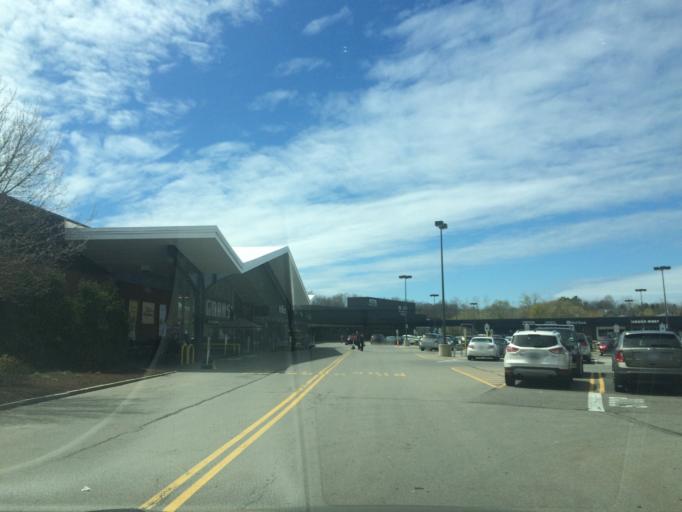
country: US
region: New York
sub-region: Monroe County
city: East Rochester
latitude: 43.1022
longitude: -77.4829
